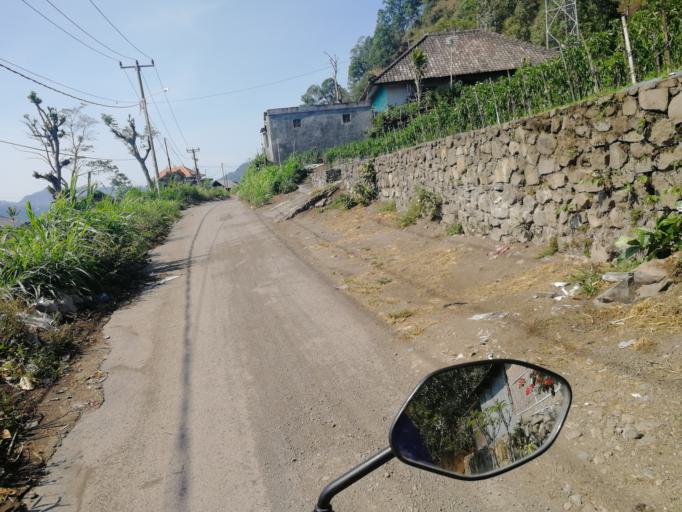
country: ID
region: Bali
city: Banjar Trunyan
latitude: -8.2602
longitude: 115.4232
